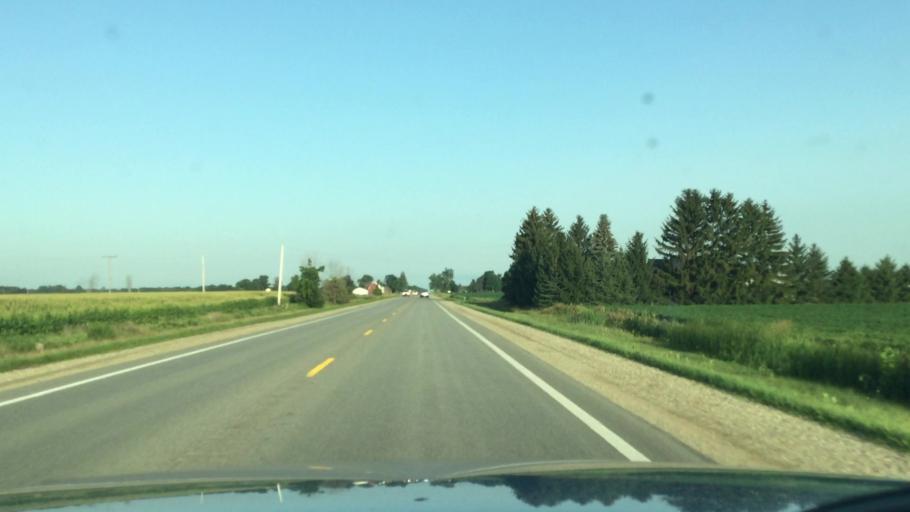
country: US
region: Michigan
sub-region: Gratiot County
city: Ithaca
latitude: 43.1760
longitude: -84.5879
